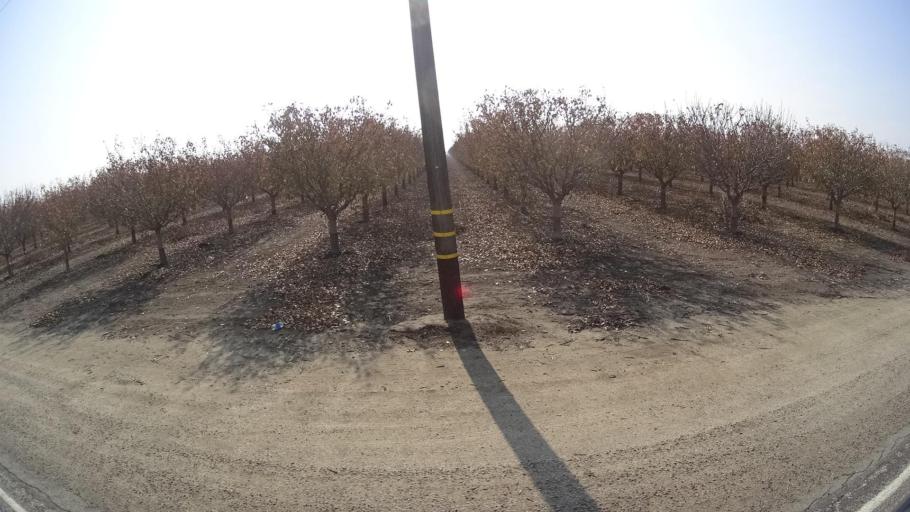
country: US
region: California
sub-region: Kern County
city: Buttonwillow
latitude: 35.3546
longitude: -119.3913
